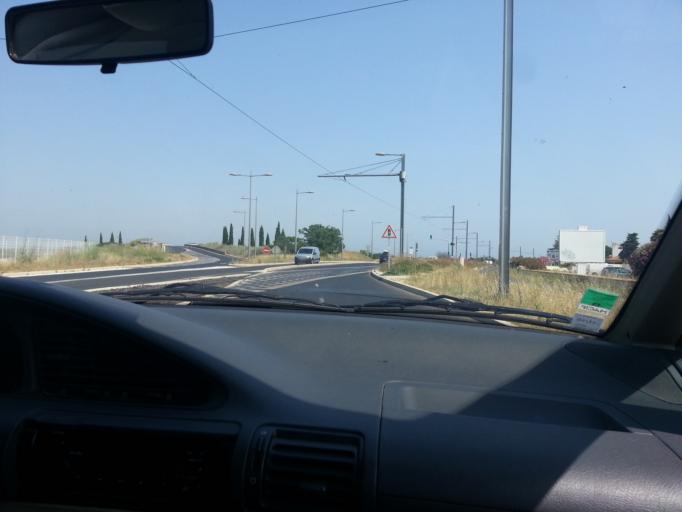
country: FR
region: Languedoc-Roussillon
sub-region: Departement de l'Herault
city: Perols
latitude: 43.5689
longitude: 3.9537
